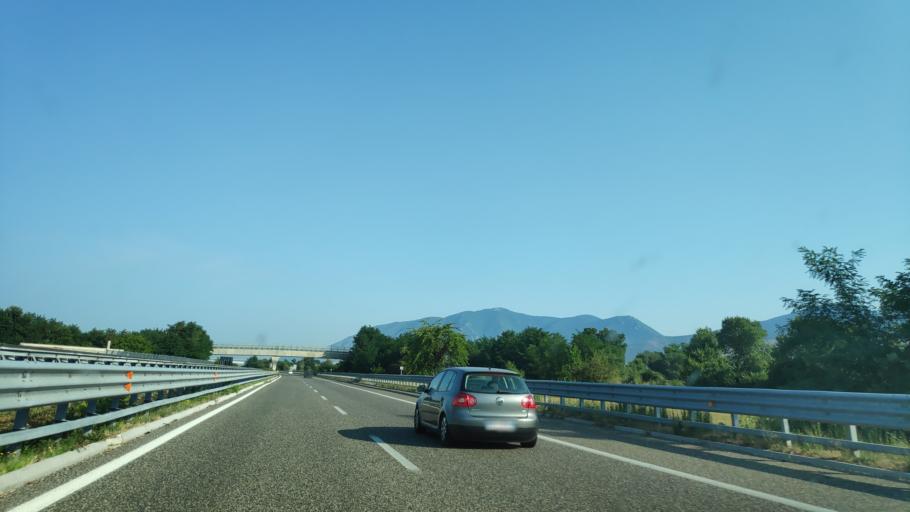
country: IT
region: Campania
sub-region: Provincia di Salerno
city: Padula
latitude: 40.3286
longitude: 15.6340
